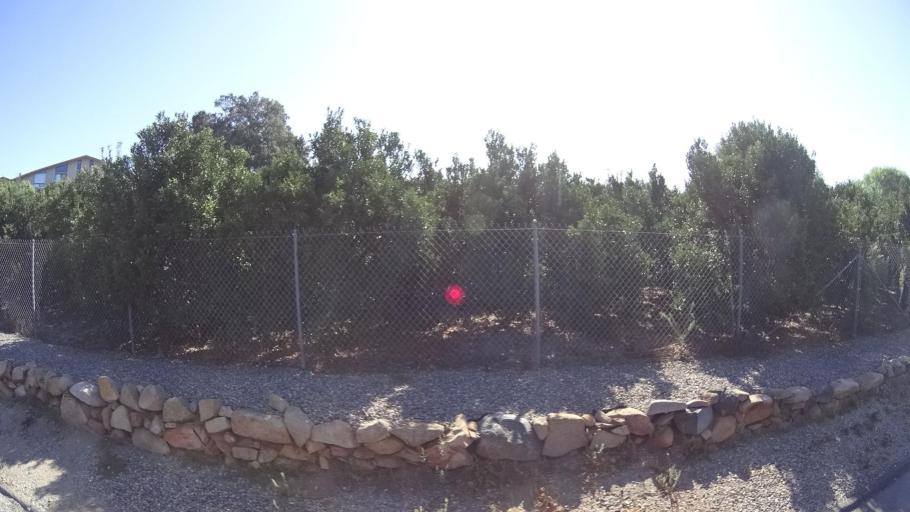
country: US
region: California
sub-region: San Diego County
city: Hidden Meadows
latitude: 33.2277
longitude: -117.1204
